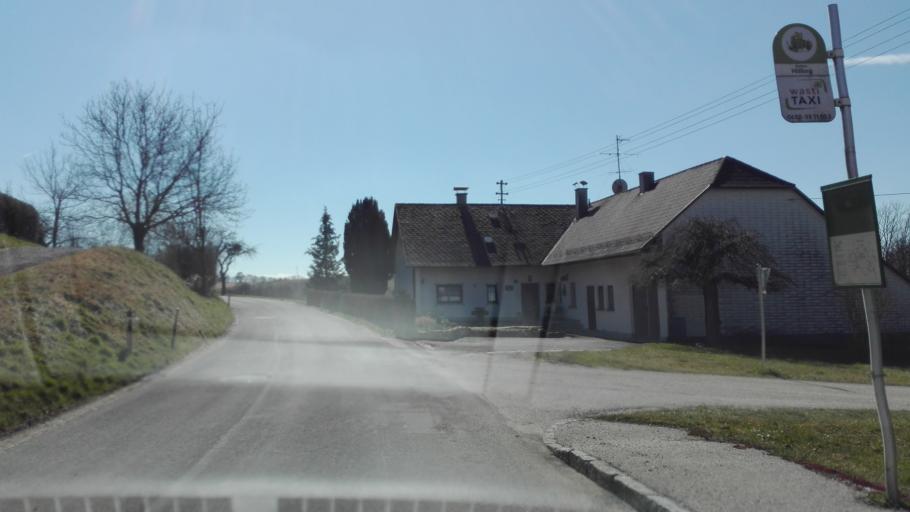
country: AT
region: Upper Austria
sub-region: Wels-Land
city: Buchkirchen
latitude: 48.2300
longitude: 13.9736
